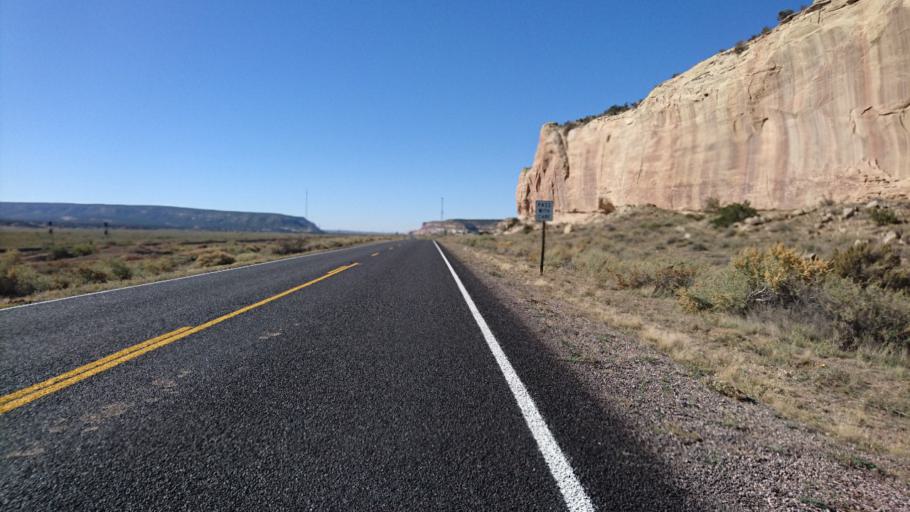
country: US
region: Arizona
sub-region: Apache County
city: Houck
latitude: 35.4024
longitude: -109.0127
